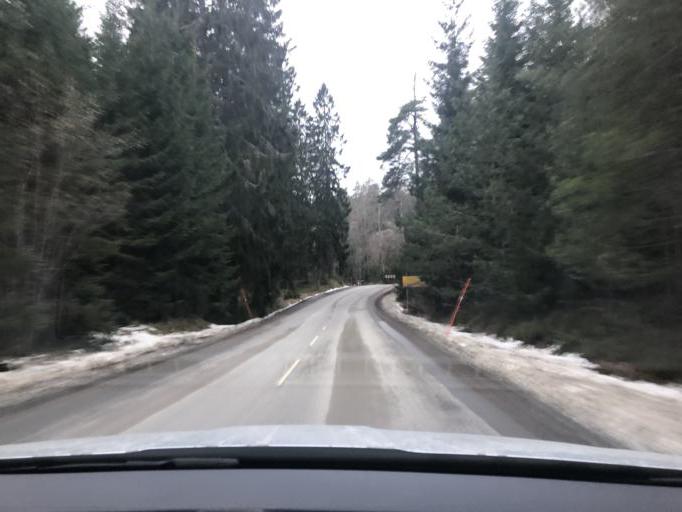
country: SE
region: Stockholm
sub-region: Botkyrka Kommun
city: Tullinge
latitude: 59.1684
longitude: 17.9084
